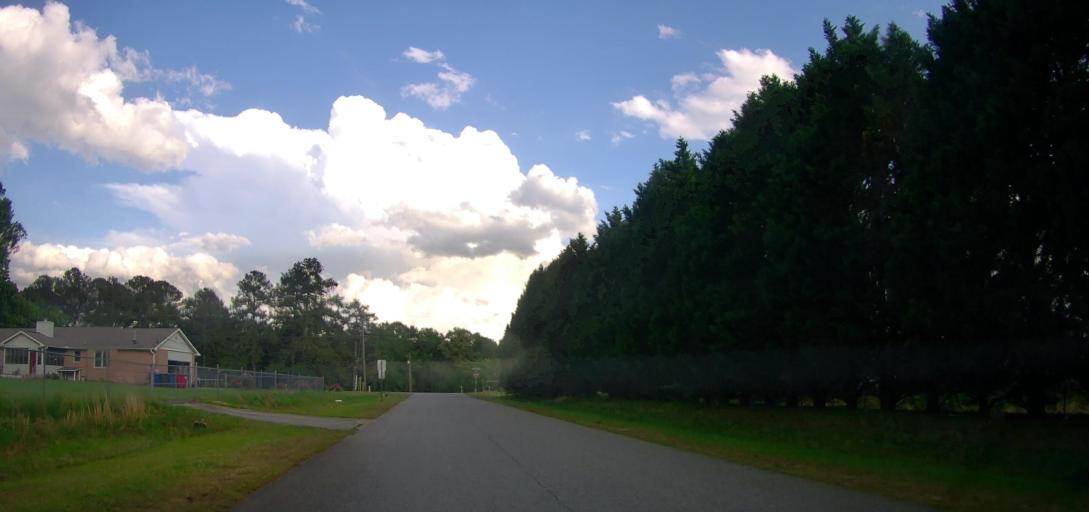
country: US
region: Georgia
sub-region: Peach County
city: Byron
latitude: 32.7344
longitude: -83.7395
